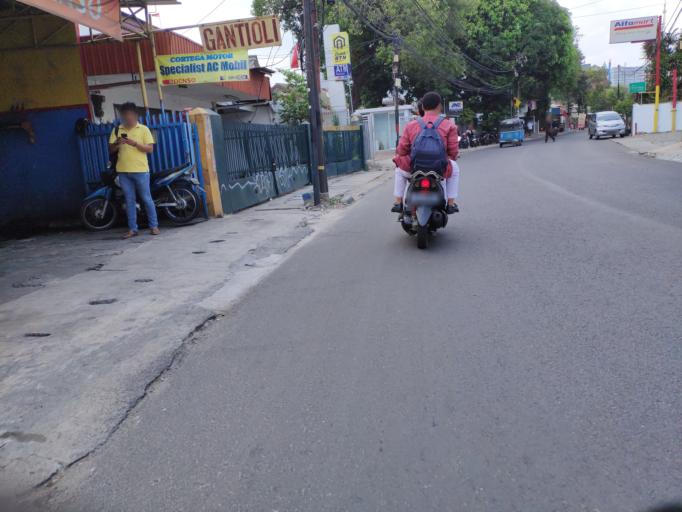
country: ID
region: Jakarta Raya
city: Jakarta
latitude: -6.1963
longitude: 106.8708
